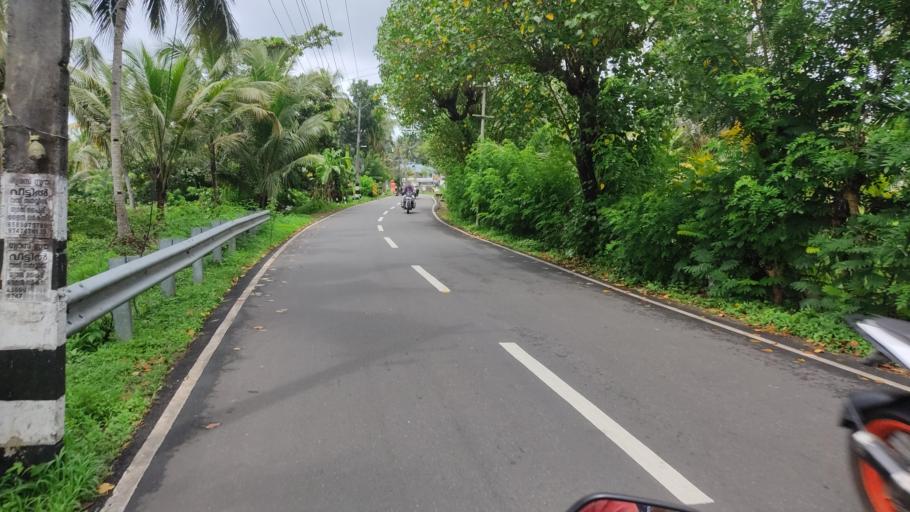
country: IN
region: Kerala
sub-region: Alappuzha
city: Kayankulam
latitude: 9.1659
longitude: 76.4931
